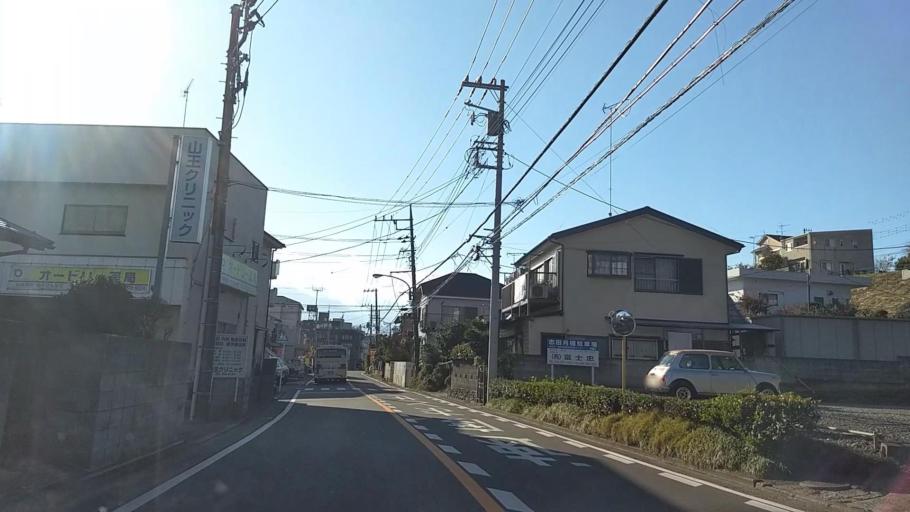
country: JP
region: Kanagawa
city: Yokohama
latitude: 35.5203
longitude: 139.5665
